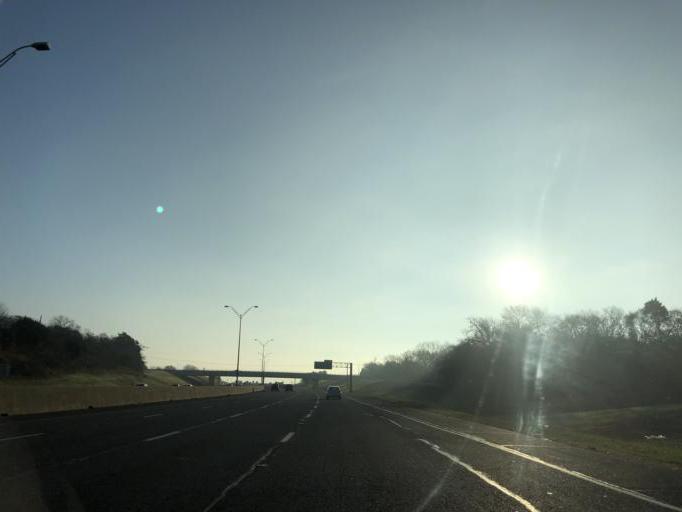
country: US
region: Texas
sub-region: Dallas County
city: Duncanville
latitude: 32.6672
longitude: -96.9197
